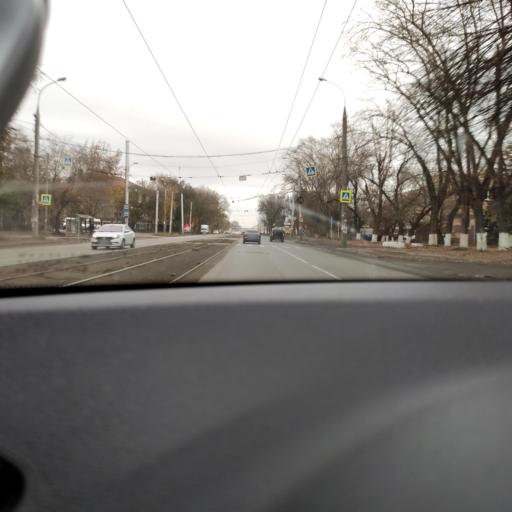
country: RU
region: Samara
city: Smyshlyayevka
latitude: 53.1963
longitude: 50.2897
